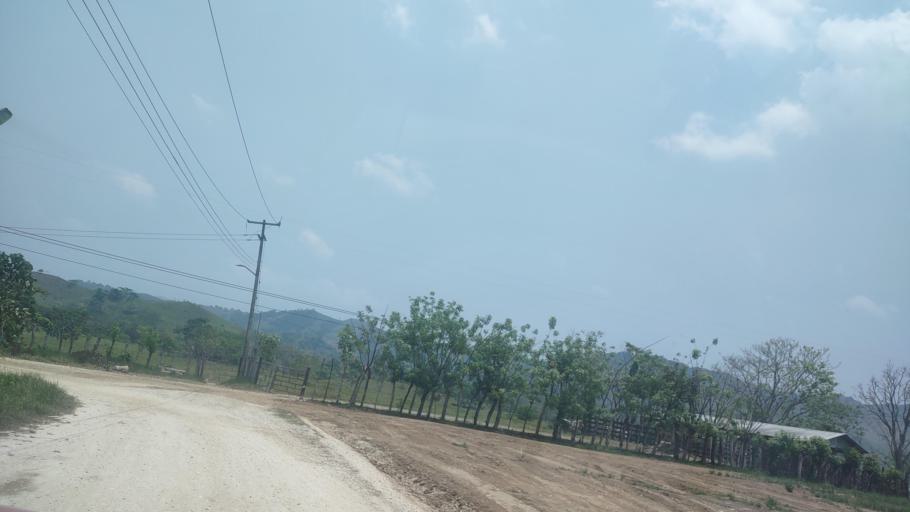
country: MX
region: Chiapas
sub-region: Tecpatan
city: Raudales Malpaso
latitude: 17.4601
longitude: -93.7984
